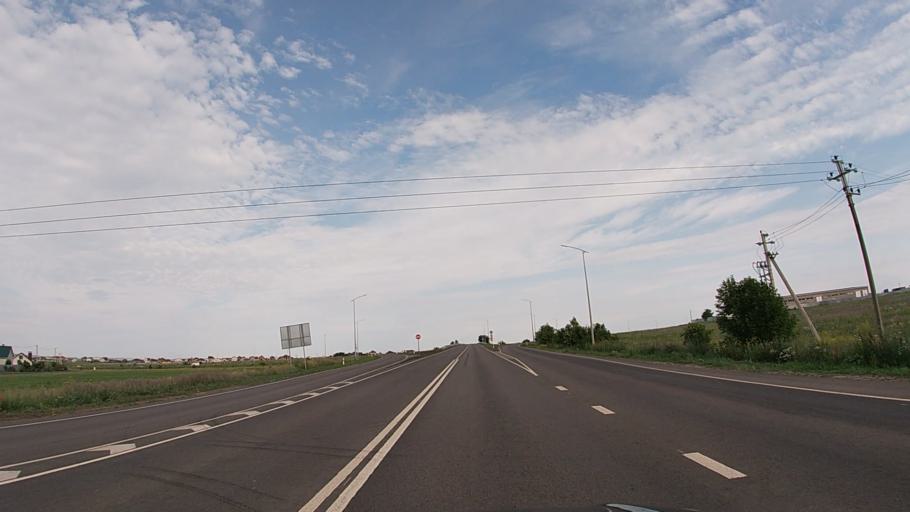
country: RU
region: Belgorod
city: Severnyy
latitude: 50.6729
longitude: 36.4783
